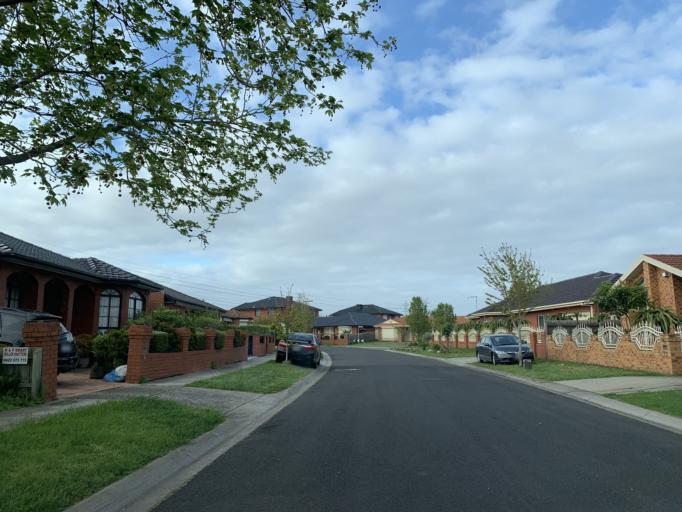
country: AU
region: Victoria
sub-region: Brimbank
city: Sunshine North
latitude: -37.7555
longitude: 144.8219
